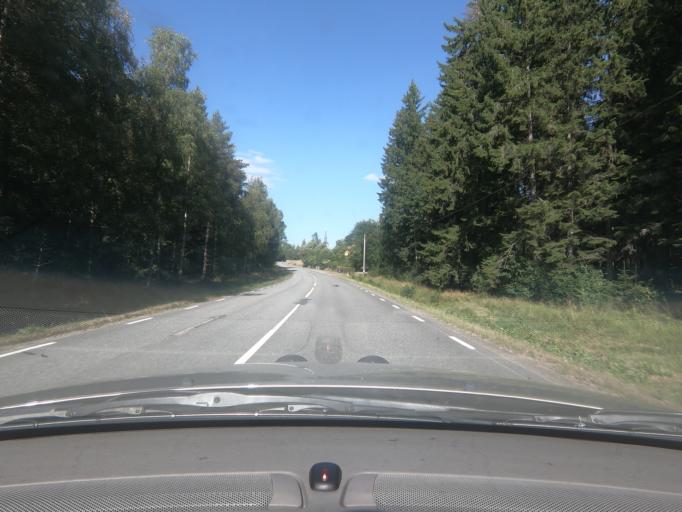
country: SE
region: Joenkoeping
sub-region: Vetlanda Kommun
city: Landsbro
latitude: 57.3746
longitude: 14.9311
